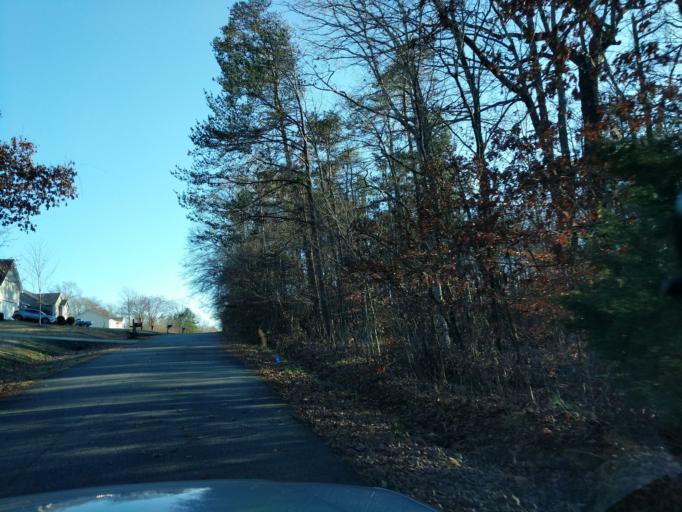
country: US
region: South Carolina
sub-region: Spartanburg County
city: Duncan
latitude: 34.9245
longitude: -82.1270
